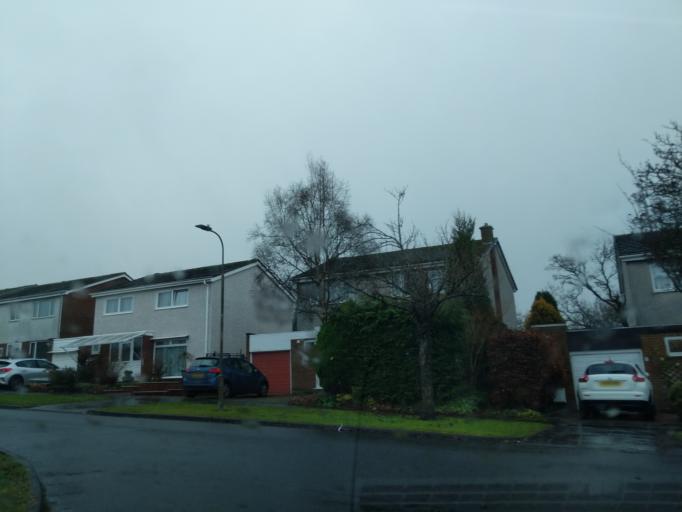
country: GB
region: Scotland
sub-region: Edinburgh
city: Balerno
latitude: 55.8768
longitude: -3.3415
